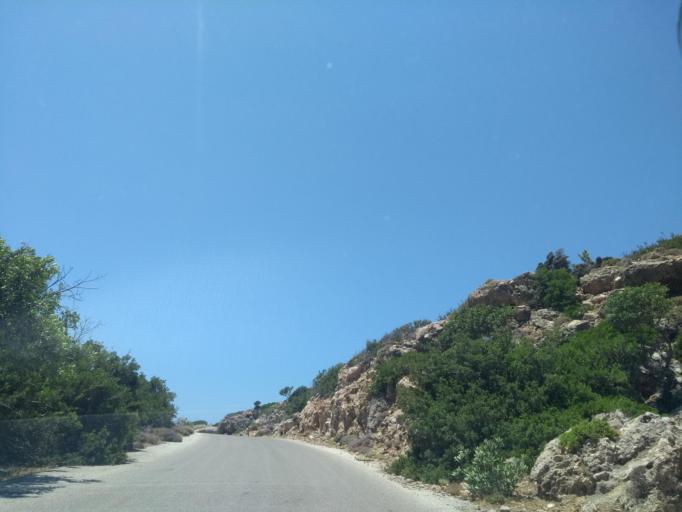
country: GR
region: Crete
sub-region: Nomos Chanias
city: Vryses
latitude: 35.3306
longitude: 23.5472
